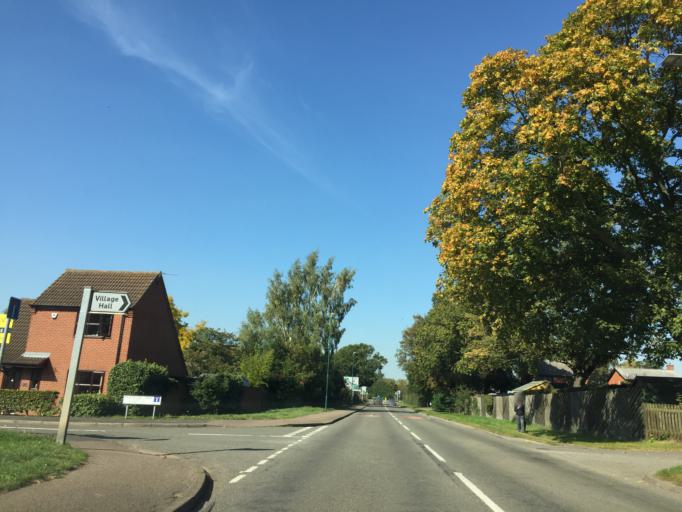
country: GB
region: England
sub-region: Leicestershire
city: Queniborough
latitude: 52.7072
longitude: -1.0498
